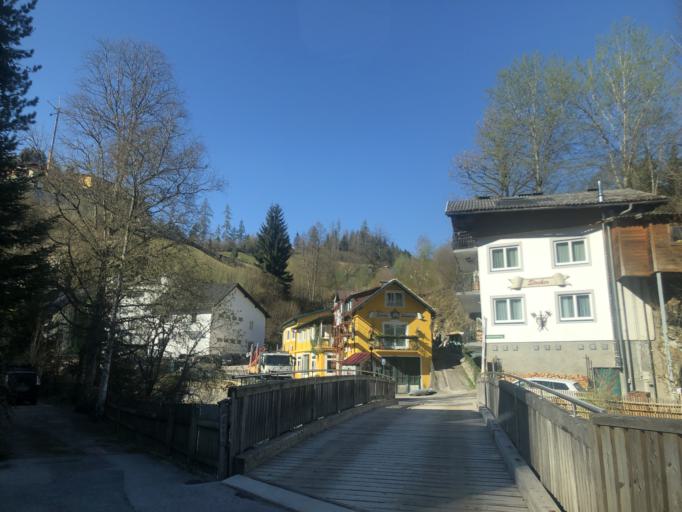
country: AT
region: Styria
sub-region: Politischer Bezirk Liezen
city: Schladming
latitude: 47.3890
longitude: 13.6885
